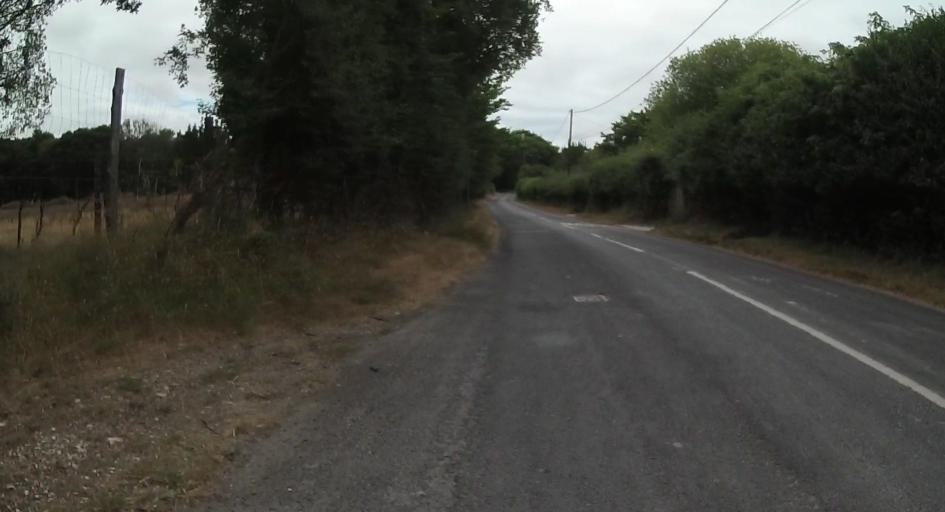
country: GB
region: England
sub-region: Dorset
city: Wareham
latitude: 50.6540
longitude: -2.0983
